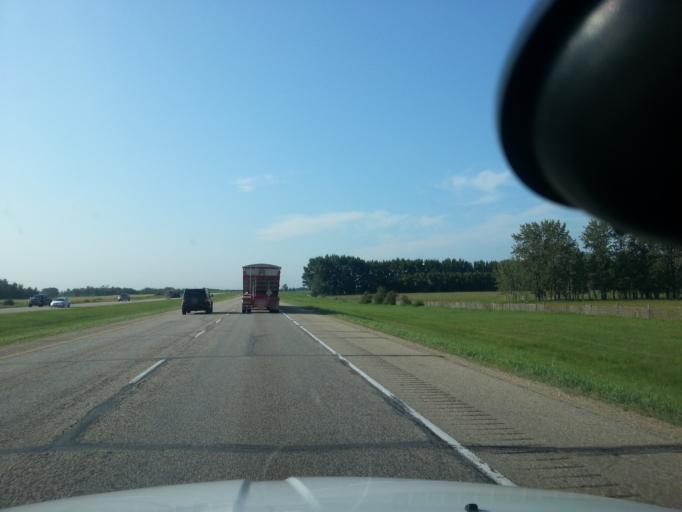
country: CA
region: Alberta
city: Millet
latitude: 52.9262
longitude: -113.6442
